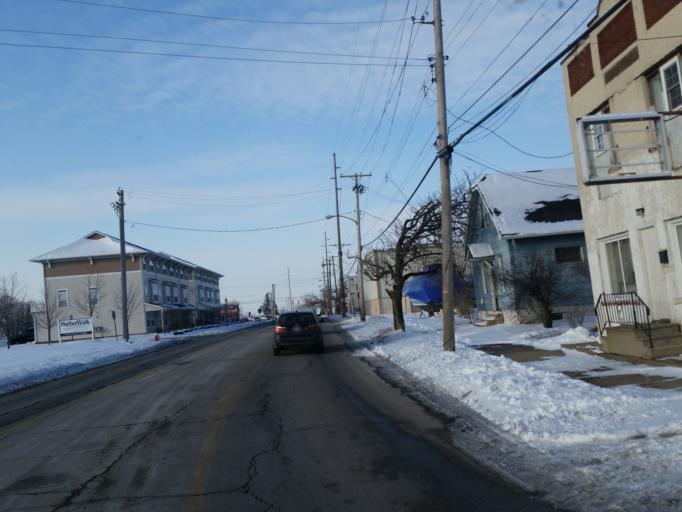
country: US
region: Ohio
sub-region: Lorain County
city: Lorain
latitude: 41.4699
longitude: -82.1695
